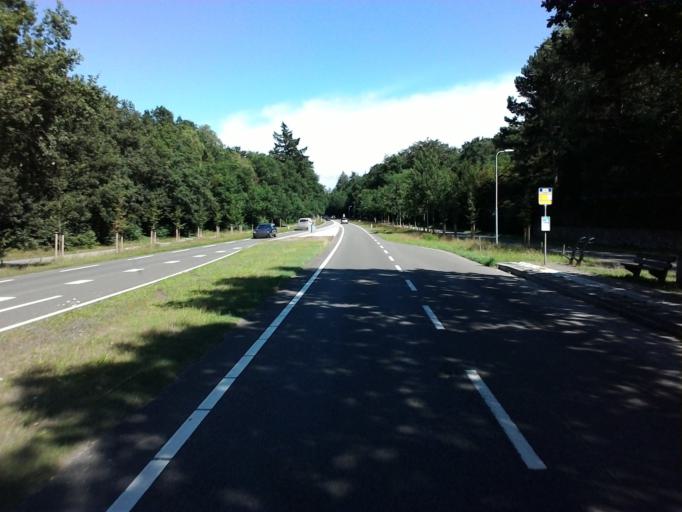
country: NL
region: Utrecht
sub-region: Gemeente Baarn
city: Baarn
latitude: 52.2017
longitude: 5.2539
